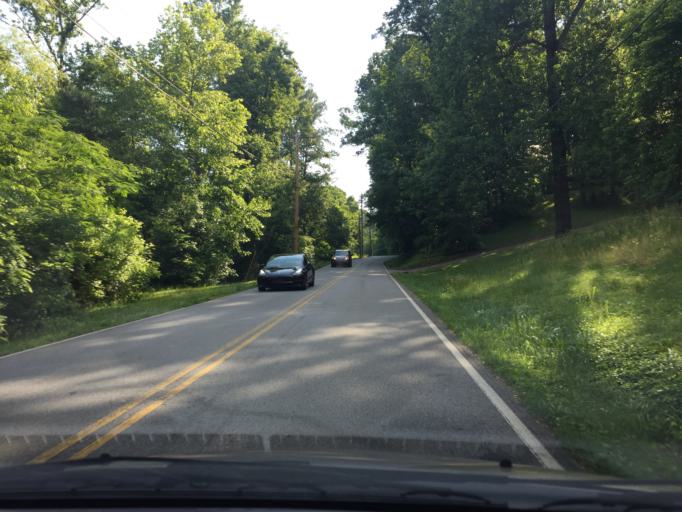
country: US
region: Tennessee
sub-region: Hamilton County
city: Collegedale
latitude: 35.0542
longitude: -85.0395
